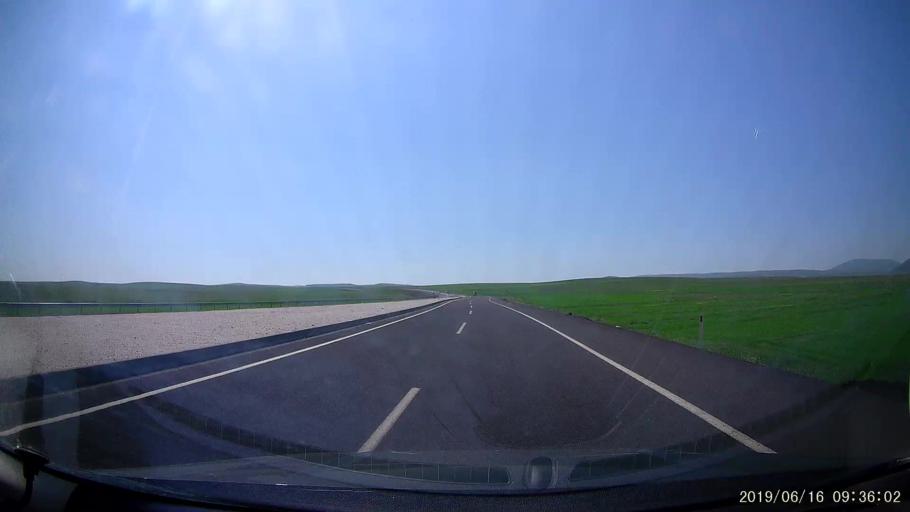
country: TR
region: Kars
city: Kars
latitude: 40.5627
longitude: 43.1655
